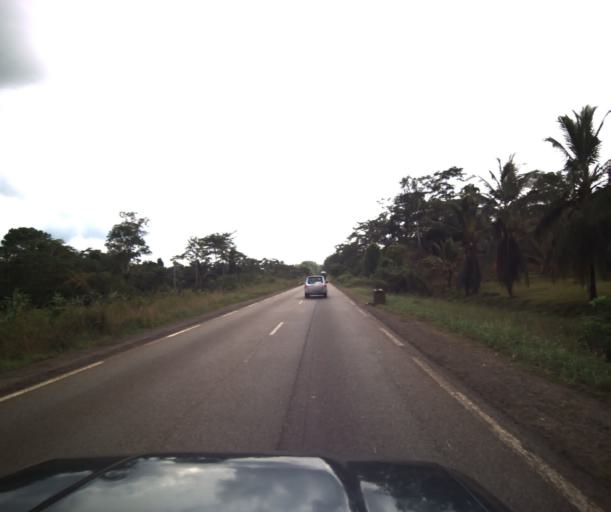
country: CM
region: Littoral
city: Edea
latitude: 3.8139
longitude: 10.3188
